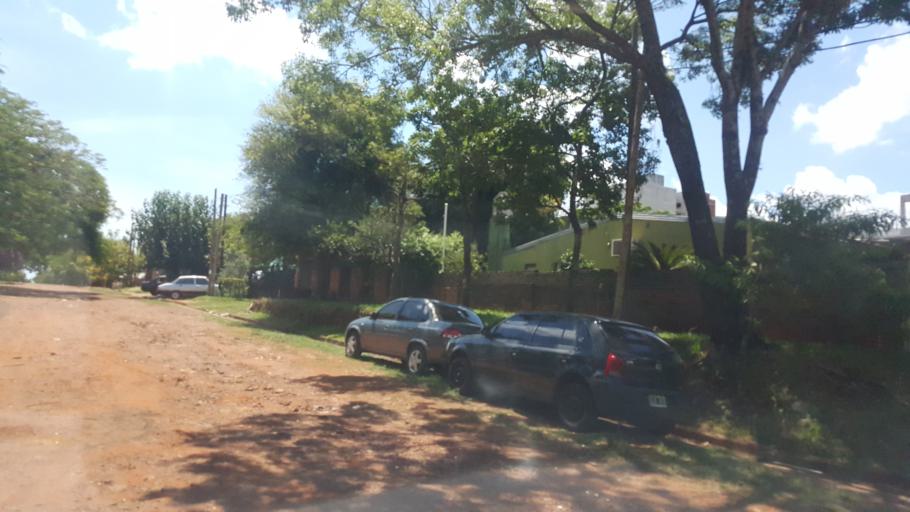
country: AR
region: Misiones
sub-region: Departamento de Capital
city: Posadas
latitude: -27.3695
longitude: -55.9208
